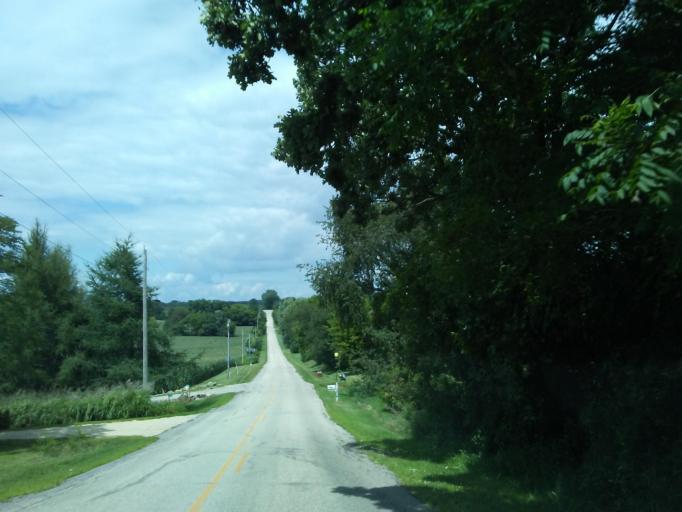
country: US
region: Wisconsin
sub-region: Dane County
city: Verona
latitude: 43.0050
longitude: -89.5782
